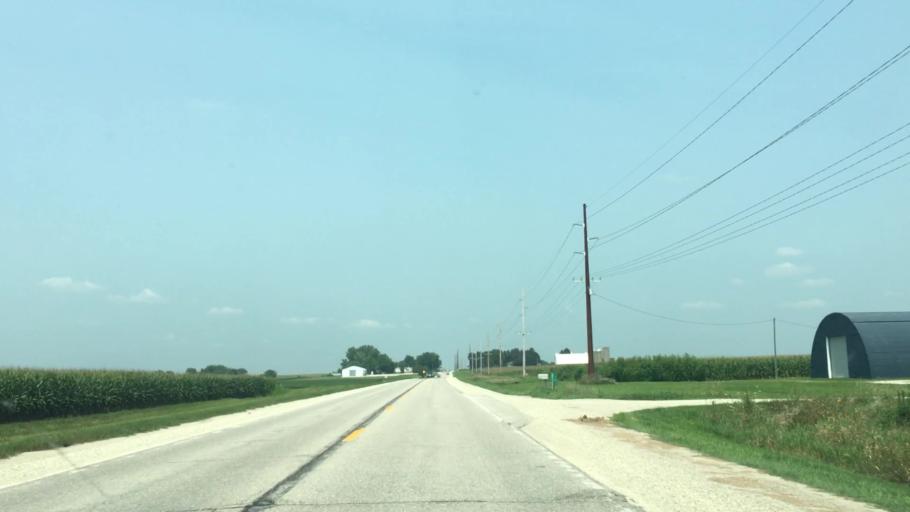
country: US
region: Iowa
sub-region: Buchanan County
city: Independence
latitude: 42.4135
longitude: -91.8899
